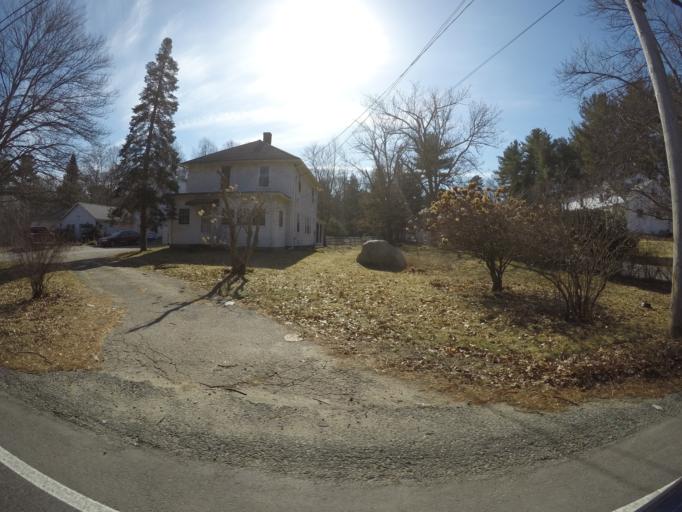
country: US
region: Massachusetts
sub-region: Plymouth County
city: Brockton
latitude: 42.0693
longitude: -71.0732
